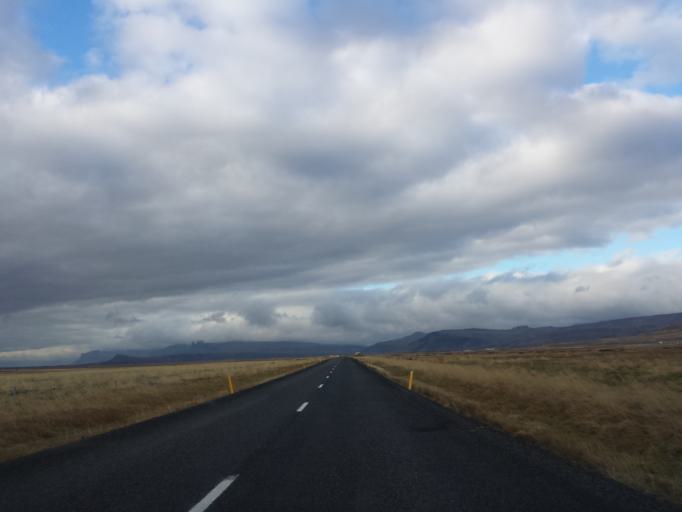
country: IS
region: West
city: Stykkisholmur
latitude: 64.8328
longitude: -22.5440
